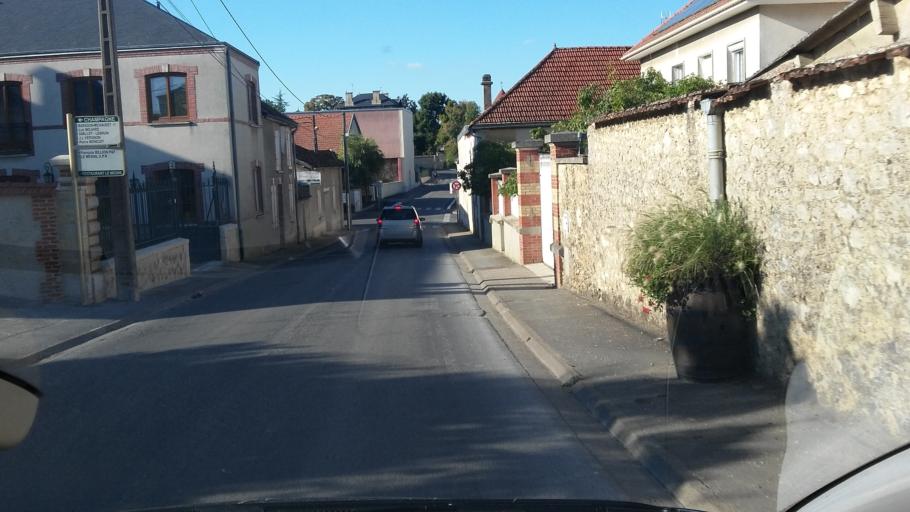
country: FR
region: Champagne-Ardenne
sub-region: Departement de la Marne
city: Le Mesnil-sur-Oger
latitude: 48.9474
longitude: 4.0257
